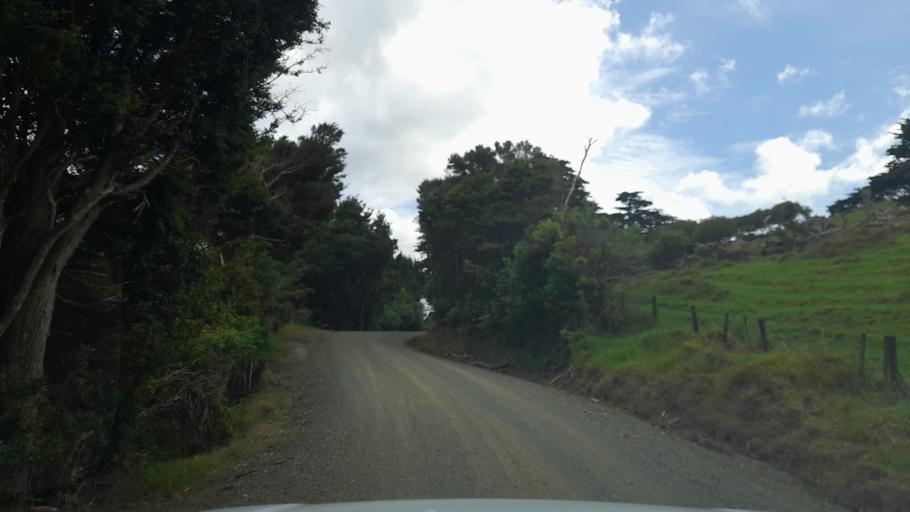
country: NZ
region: Auckland
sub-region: Auckland
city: Wellsford
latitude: -36.2160
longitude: 174.3201
